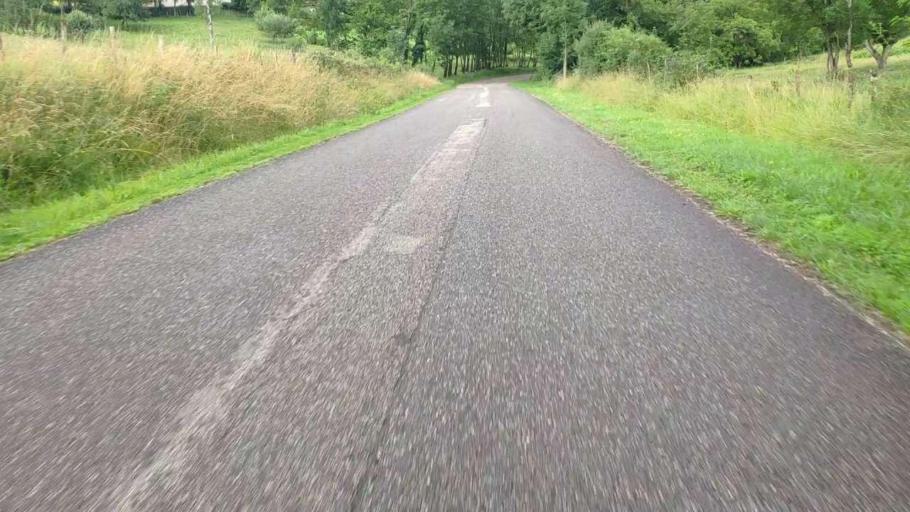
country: FR
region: Franche-Comte
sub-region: Departement du Jura
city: Poligny
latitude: 46.8018
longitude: 5.6179
